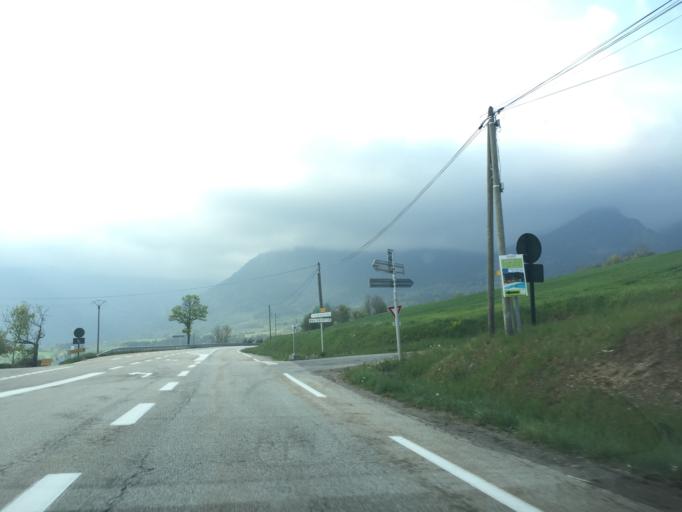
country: FR
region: Rhone-Alpes
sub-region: Departement de l'Isere
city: Mens
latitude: 44.7712
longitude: 5.6619
